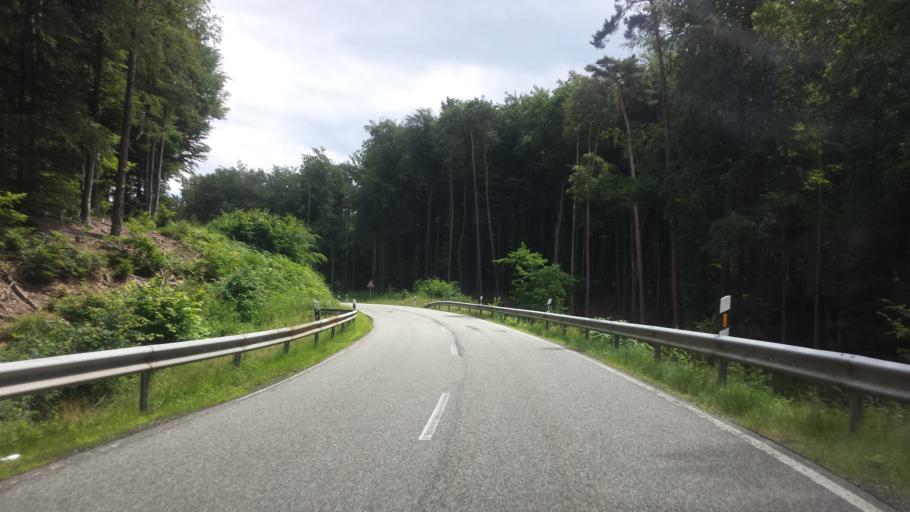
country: DE
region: Rheinland-Pfalz
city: Neuhemsbach
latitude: 49.5065
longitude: 7.9532
